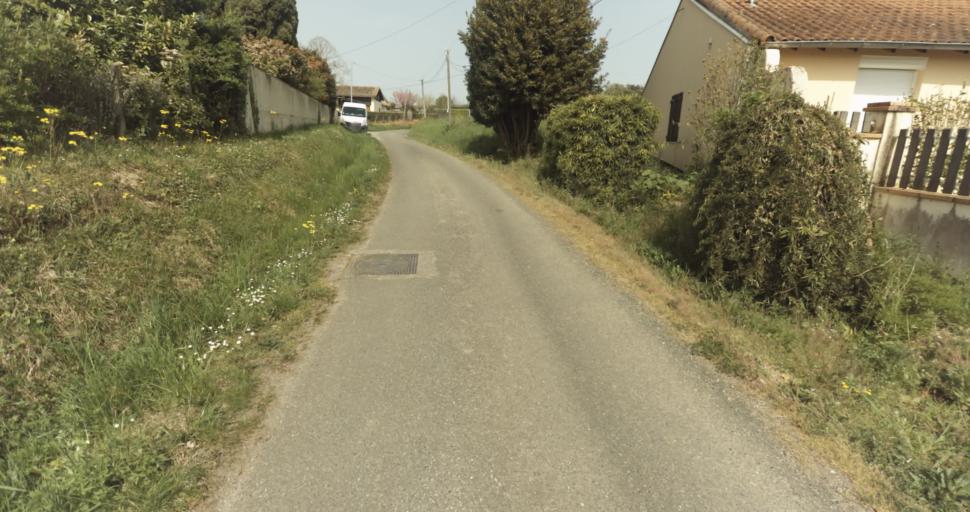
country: FR
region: Midi-Pyrenees
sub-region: Departement du Tarn-et-Garonne
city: Moissac
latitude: 44.1091
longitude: 1.0859
